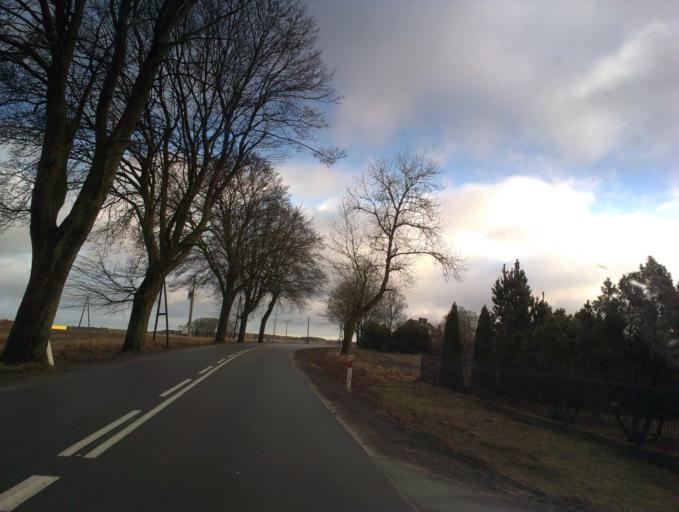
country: PL
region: Pomeranian Voivodeship
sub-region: Powiat czluchowski
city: Czarne
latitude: 53.6863
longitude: 16.9641
